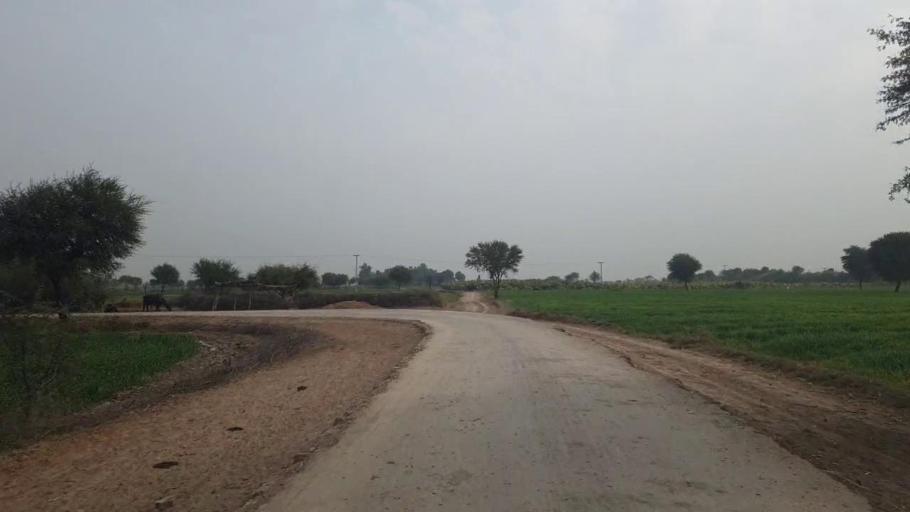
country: PK
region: Sindh
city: Shahdadpur
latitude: 25.9490
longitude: 68.7033
